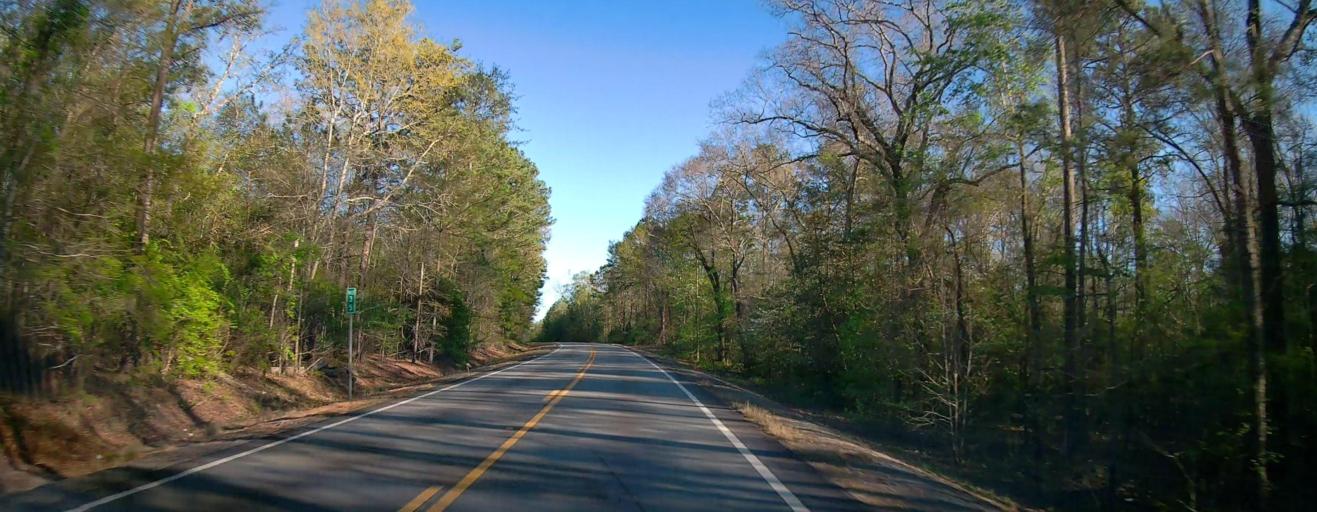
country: US
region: Georgia
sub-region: Wilkinson County
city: Irwinton
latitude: 32.9375
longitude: -83.1508
